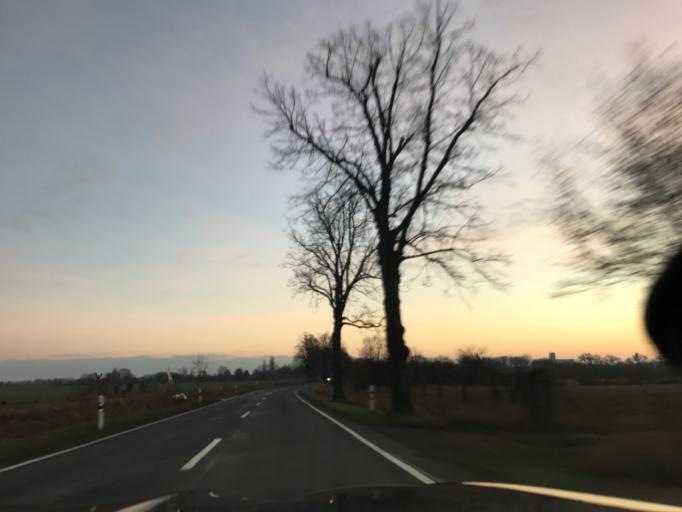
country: DE
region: Brandenburg
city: Ketzin
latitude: 52.4947
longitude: 12.8508
